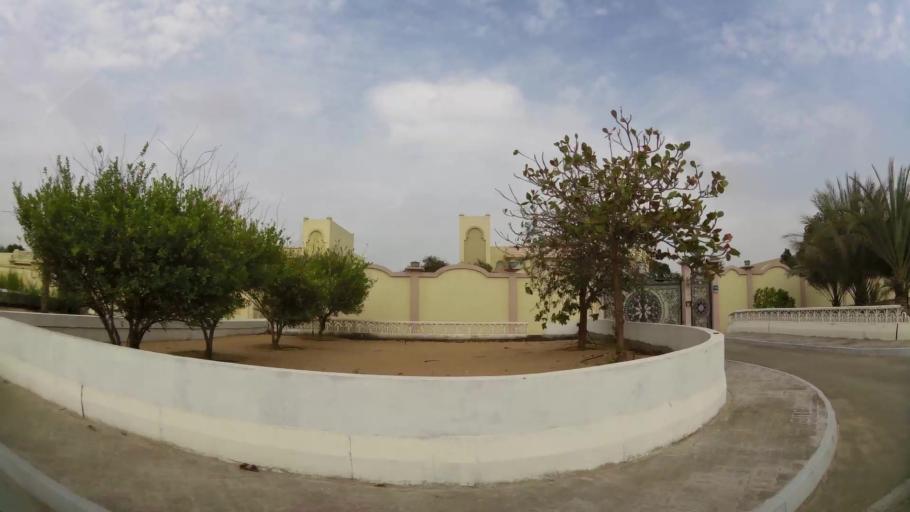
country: AE
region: Abu Dhabi
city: Abu Dhabi
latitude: 24.6402
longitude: 54.7263
